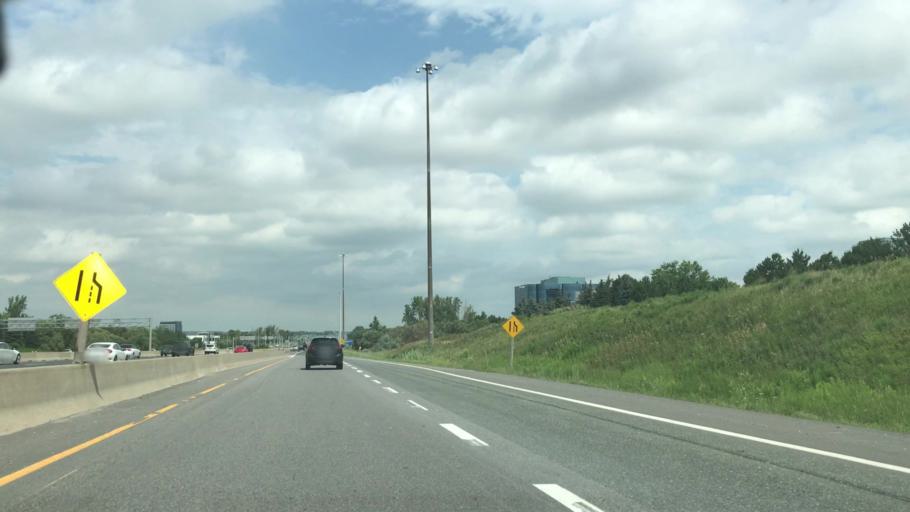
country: CA
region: Ontario
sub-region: York
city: Richmond Hill
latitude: 43.8508
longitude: -79.3714
